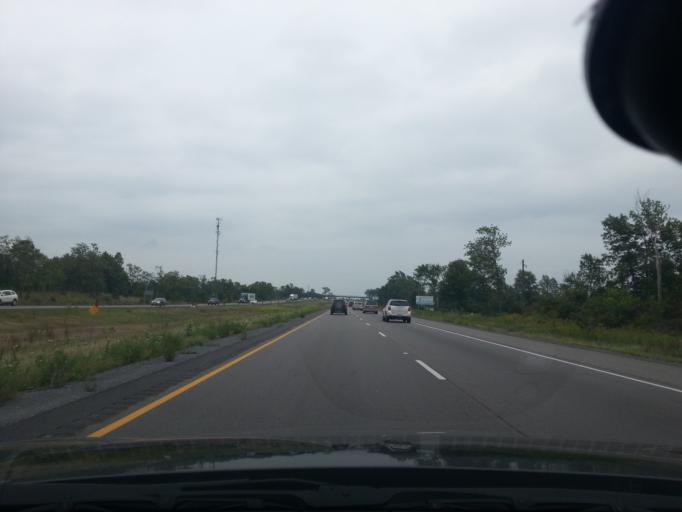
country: CA
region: Ontario
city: Kingston
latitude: 44.2865
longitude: -76.6380
